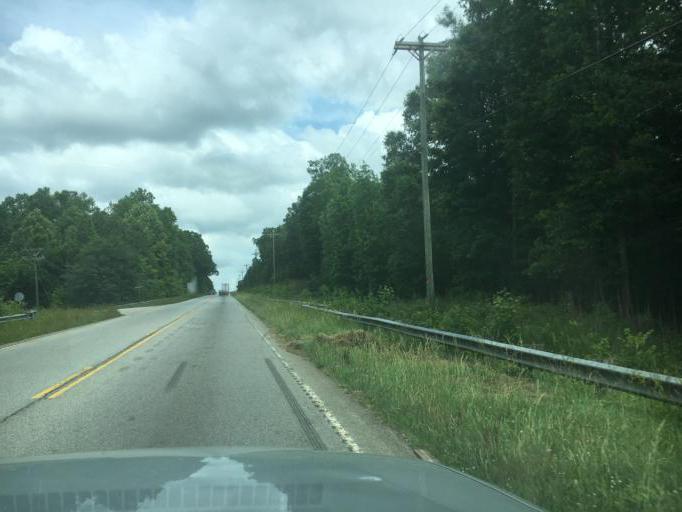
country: US
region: South Carolina
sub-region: Anderson County
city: Williamston
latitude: 34.6370
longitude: -82.4219
